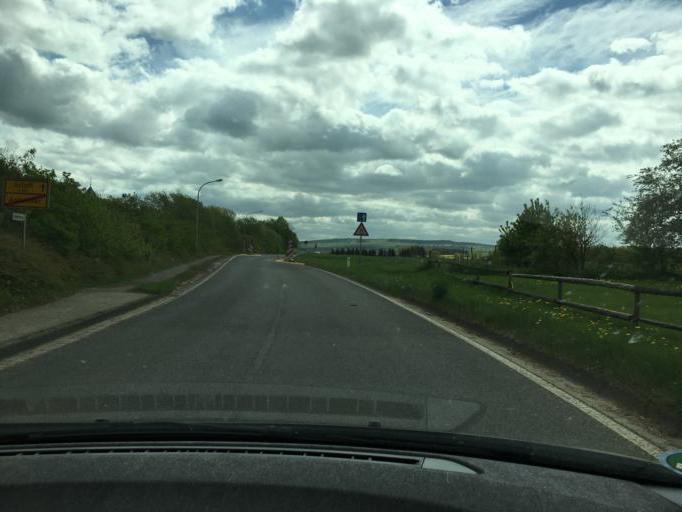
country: DE
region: North Rhine-Westphalia
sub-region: Regierungsbezirk Koln
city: Bad Munstereifel
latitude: 50.6046
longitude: 6.7434
